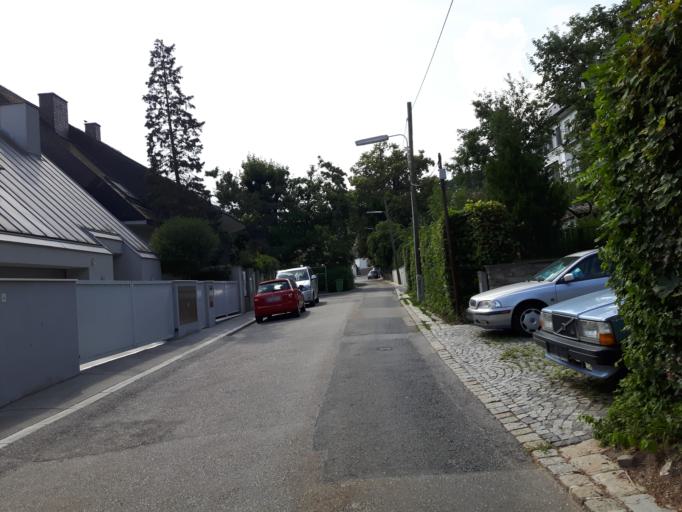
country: AT
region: Lower Austria
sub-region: Politischer Bezirk Wien-Umgebung
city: Klosterneuburg
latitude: 48.2542
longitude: 16.2932
